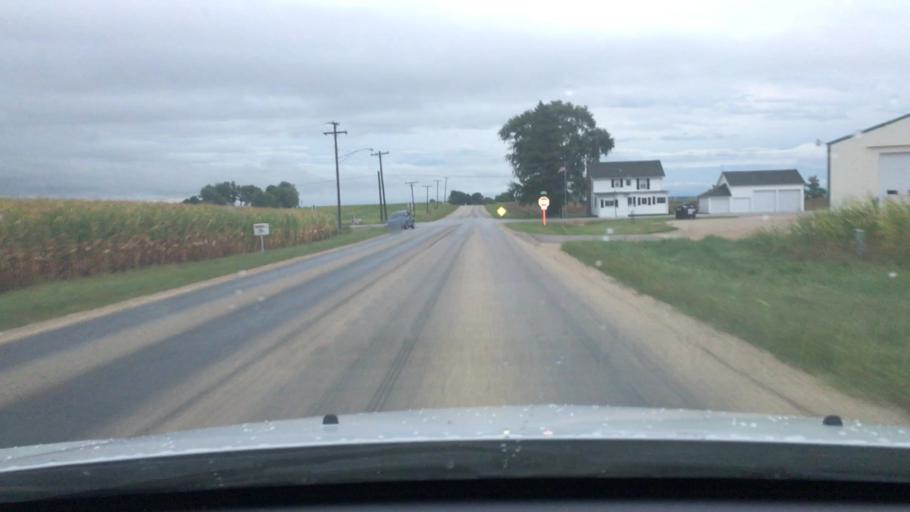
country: US
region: Illinois
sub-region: DeKalb County
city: Malta
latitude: 41.8488
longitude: -88.8876
